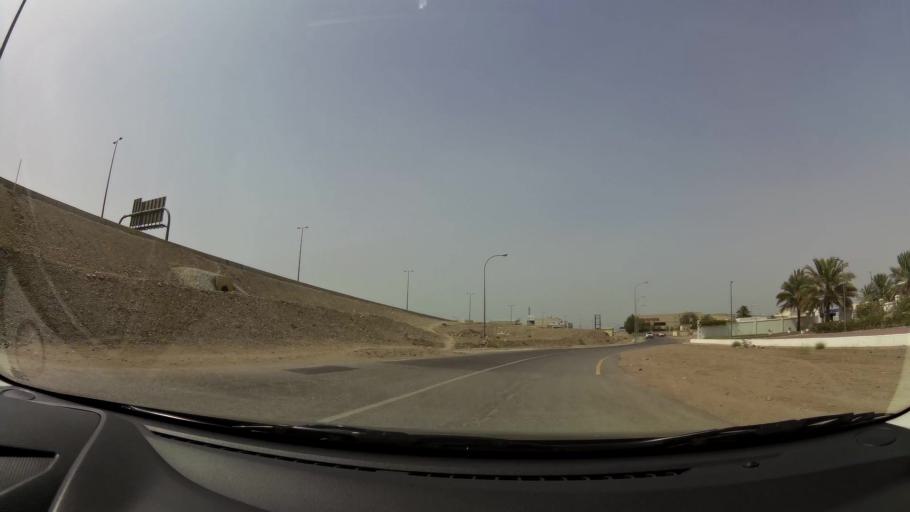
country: OM
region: Muhafazat Masqat
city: Bawshar
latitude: 23.5691
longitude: 58.3802
